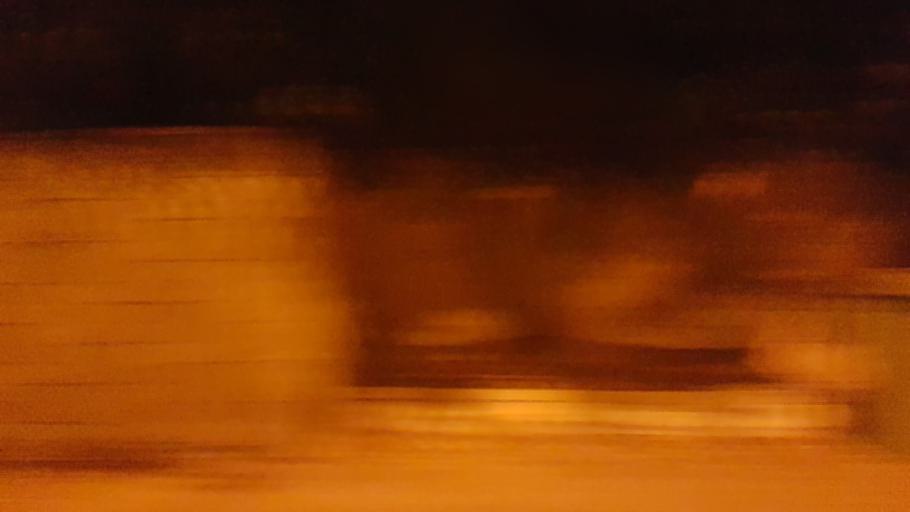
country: IL
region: Central District
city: Hod HaSharon
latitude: 32.1651
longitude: 34.8939
